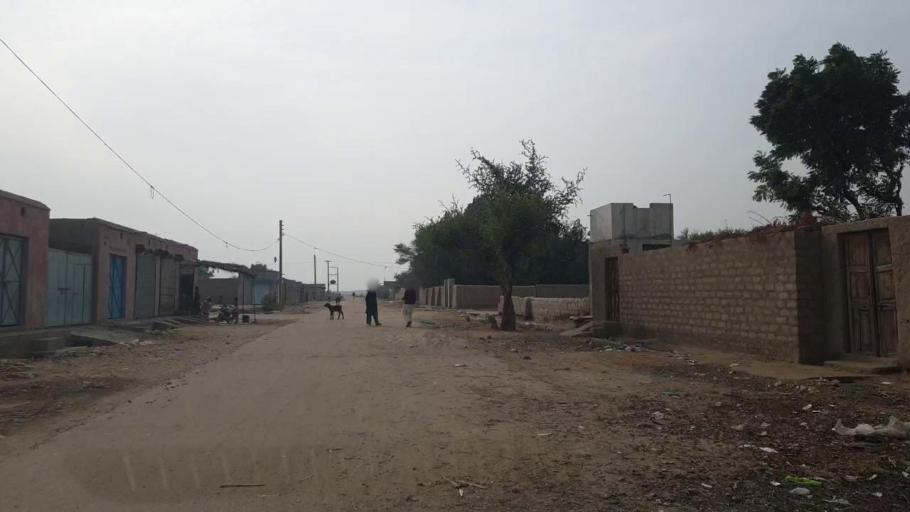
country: PK
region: Sindh
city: Sann
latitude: 26.0342
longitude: 68.1359
